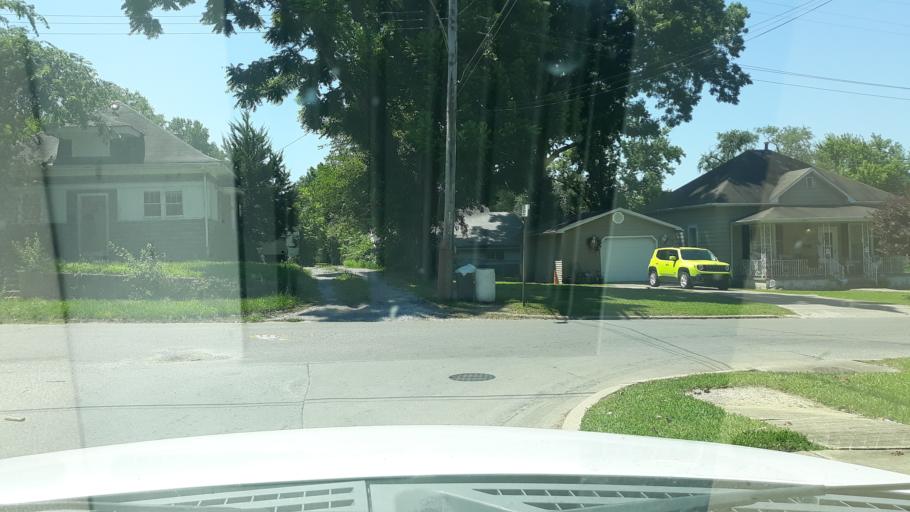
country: US
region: Illinois
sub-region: Saline County
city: Eldorado
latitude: 37.8164
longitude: -88.4349
